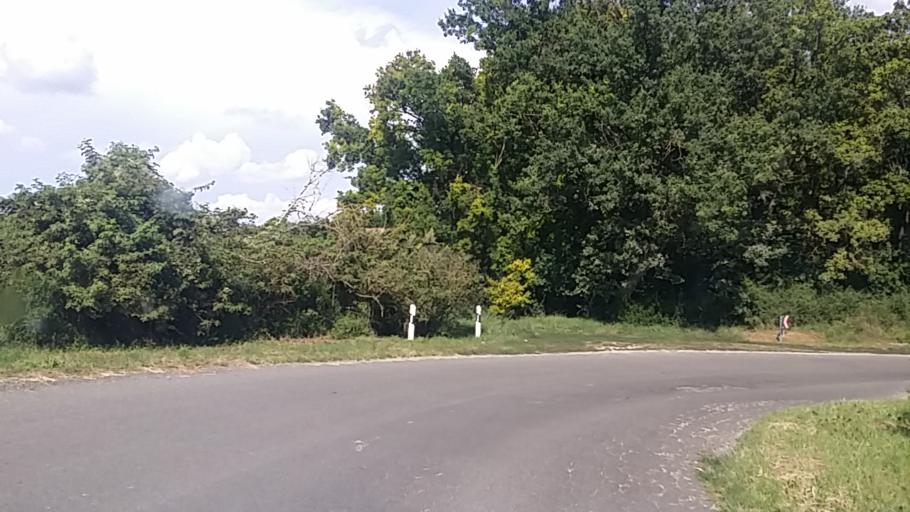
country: HU
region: Tolna
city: Gyonk
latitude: 46.5391
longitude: 18.4580
